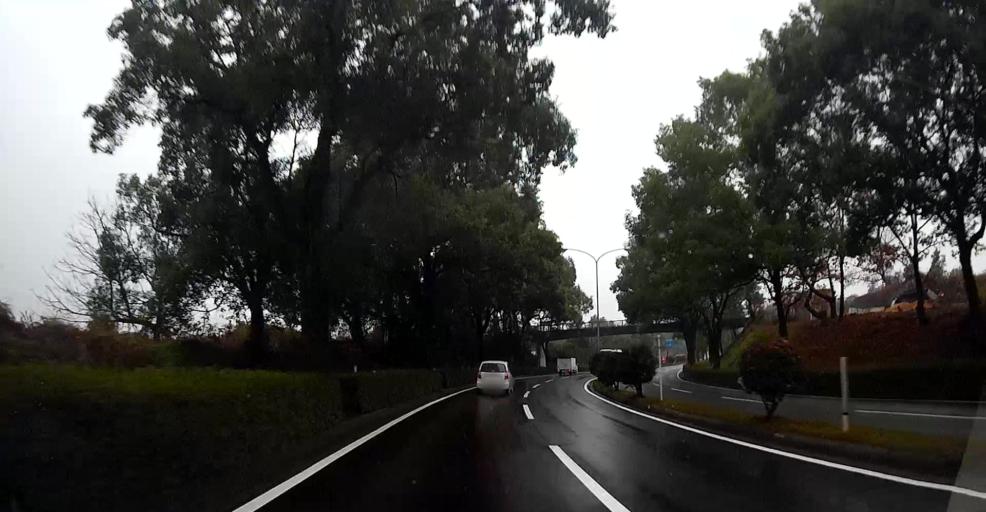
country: JP
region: Kumamoto
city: Ozu
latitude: 32.8254
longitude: 130.8591
